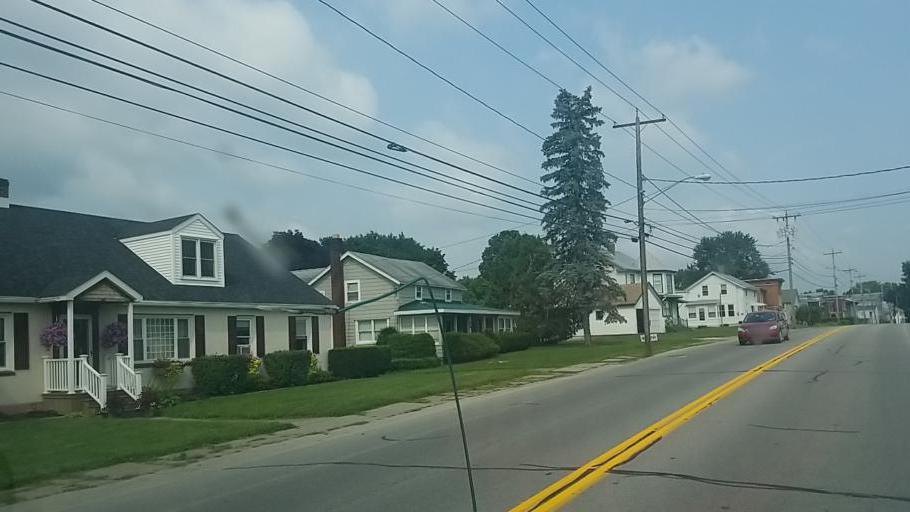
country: US
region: New York
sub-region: Montgomery County
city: Fort Plain
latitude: 42.9302
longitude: -74.6104
